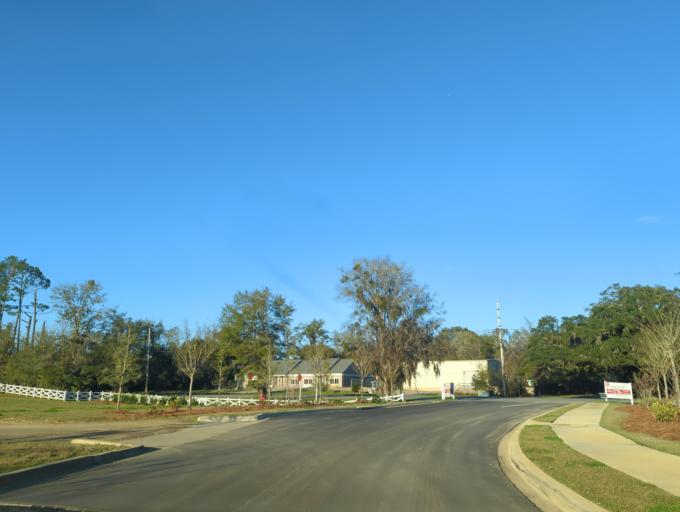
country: US
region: Florida
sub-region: Leon County
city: Tallahassee
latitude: 30.5181
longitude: -84.3492
